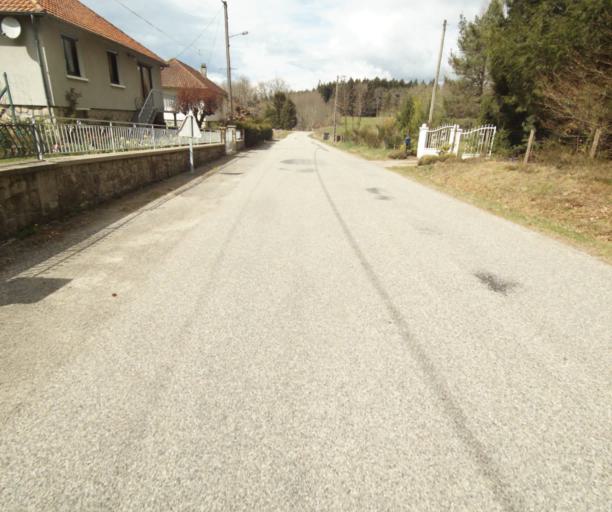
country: FR
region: Limousin
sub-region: Departement de la Correze
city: Correze
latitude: 45.2705
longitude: 1.9773
